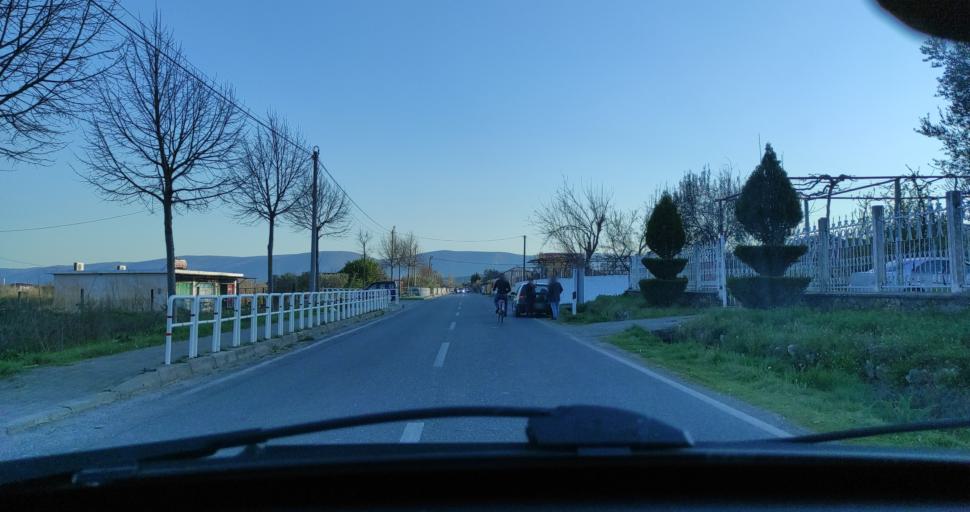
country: AL
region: Shkoder
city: Vukatane
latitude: 41.9653
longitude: 19.5382
